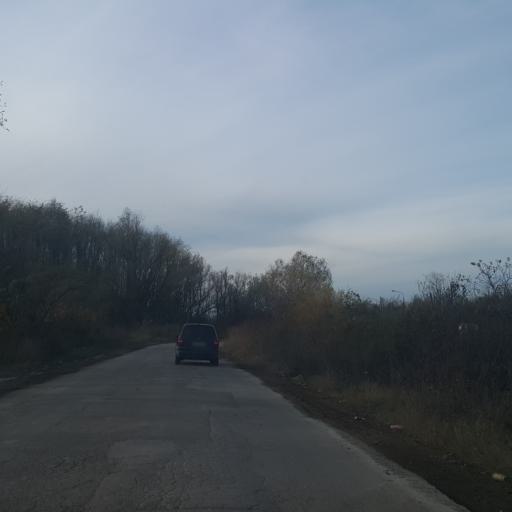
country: RS
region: Central Serbia
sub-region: Belgrade
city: Lazarevac
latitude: 44.4031
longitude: 20.3518
